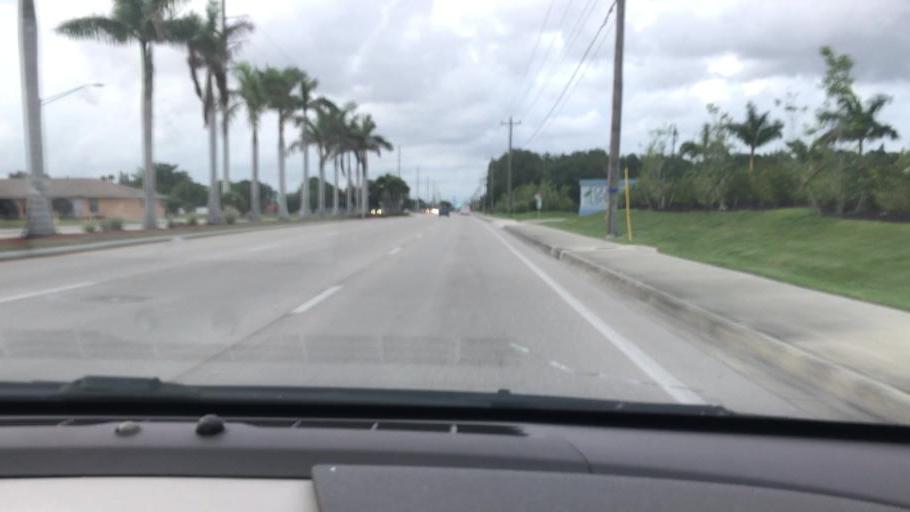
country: US
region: Florida
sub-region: Lee County
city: Cape Coral
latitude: 26.6247
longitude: -81.9742
